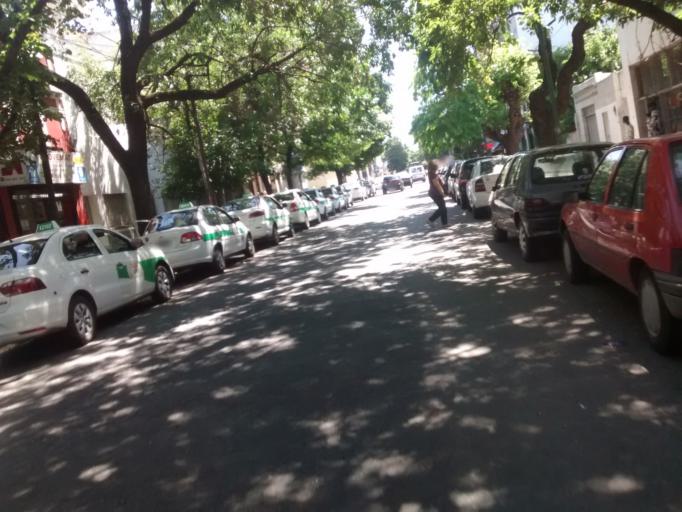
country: AR
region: Buenos Aires
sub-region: Partido de La Plata
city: La Plata
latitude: -34.9067
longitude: -57.9550
